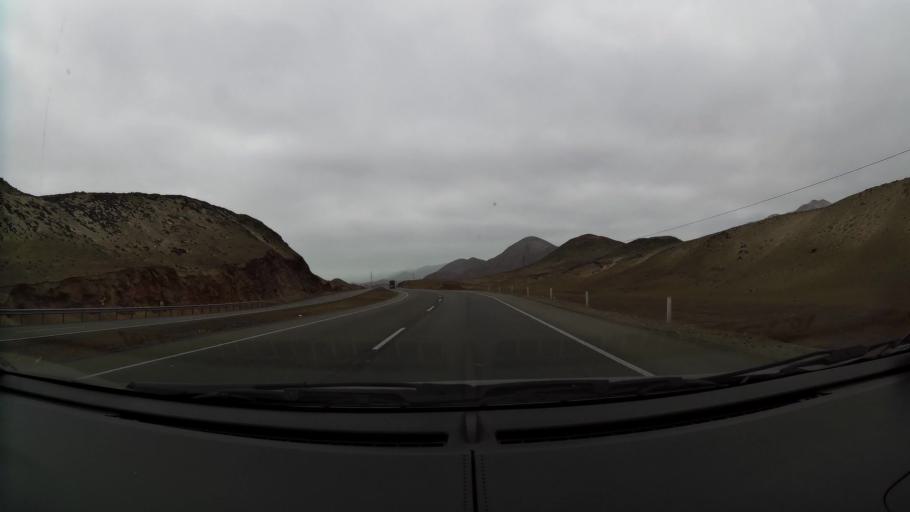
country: PE
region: Lima
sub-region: Barranca
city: Paramonga
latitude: -10.4705
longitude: -77.9155
